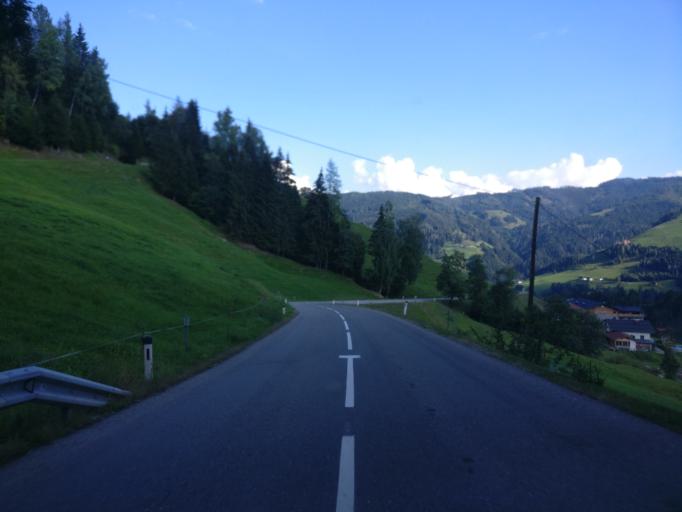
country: AT
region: Salzburg
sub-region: Politischer Bezirk Sankt Johann im Pongau
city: Muhlbach am Hochkonig
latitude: 47.3875
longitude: 13.1145
